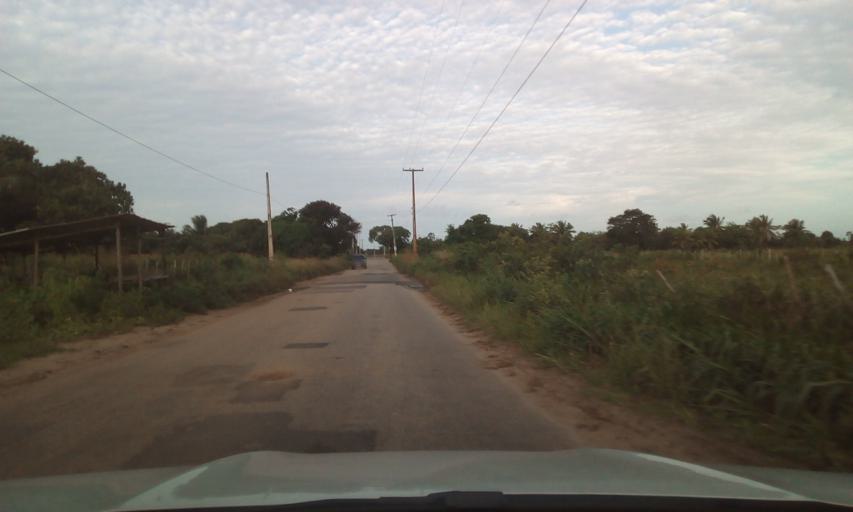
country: BR
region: Paraiba
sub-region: Conde
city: Conde
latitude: -7.2231
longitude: -34.8252
